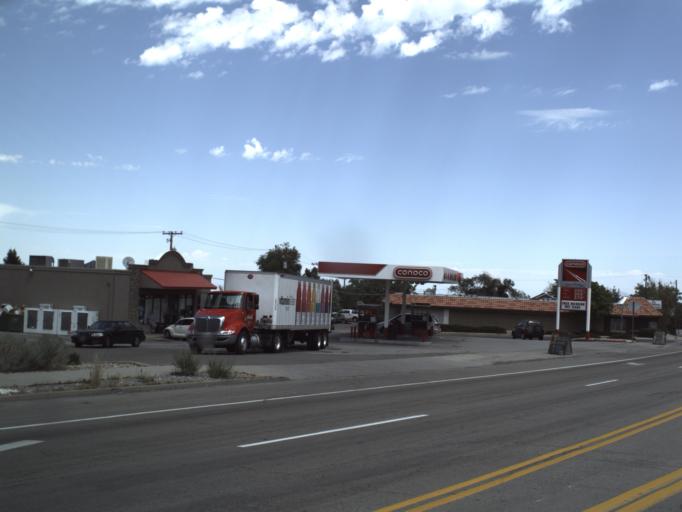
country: US
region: Utah
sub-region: Tooele County
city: Tooele
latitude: 40.5177
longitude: -112.3019
